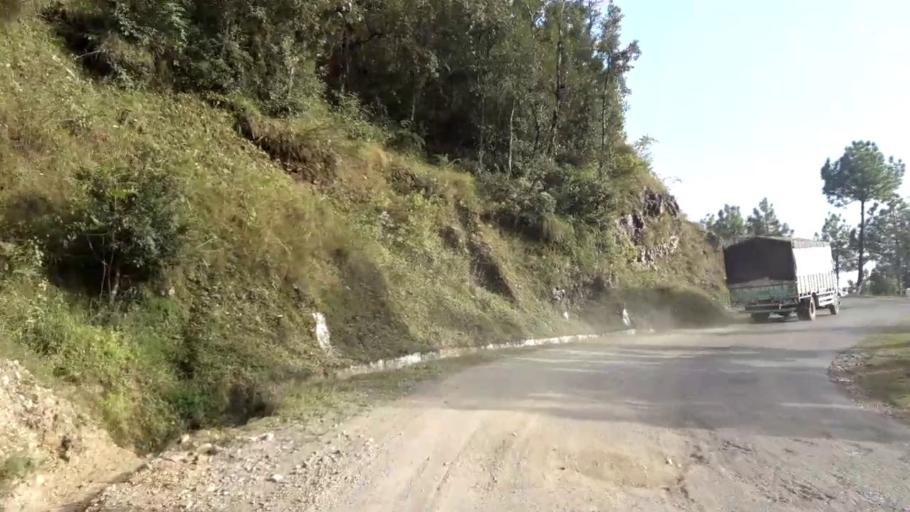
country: IN
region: Himachal Pradesh
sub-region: Shimla
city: Jutogh
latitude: 31.0492
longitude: 77.1454
